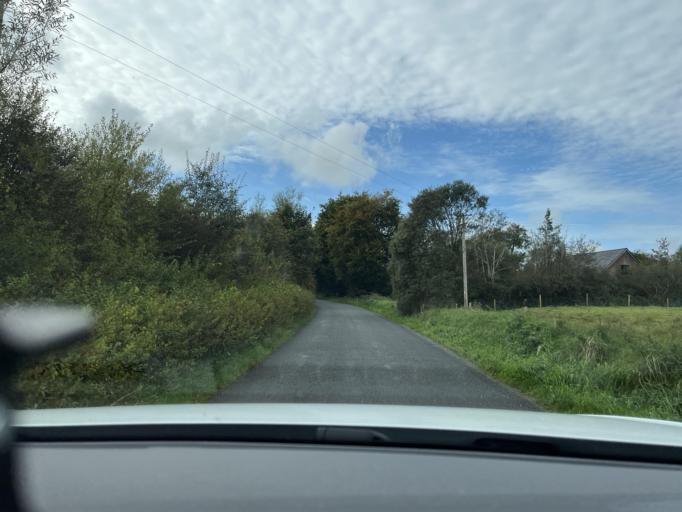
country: IE
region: Connaught
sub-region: Roscommon
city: Boyle
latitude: 54.0238
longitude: -8.3931
